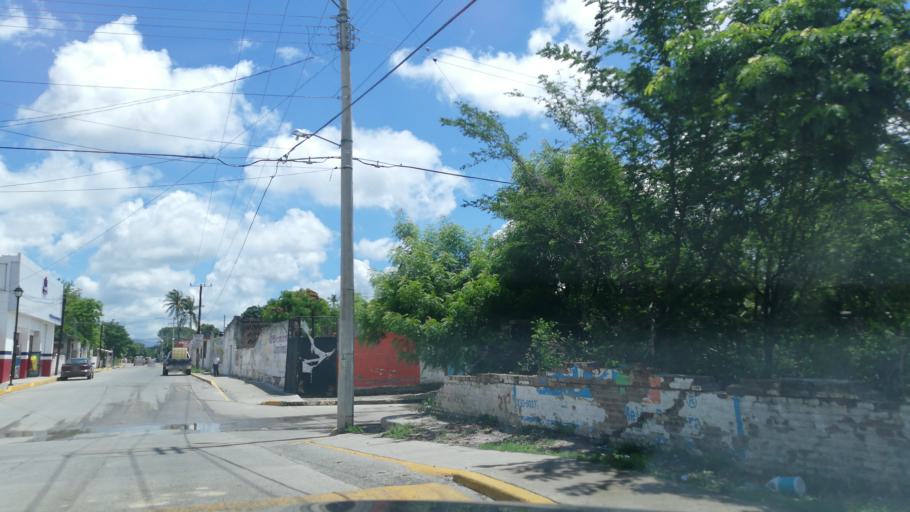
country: MX
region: Oaxaca
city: Asuncion Ixtaltepec
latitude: 16.5014
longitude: -95.0515
